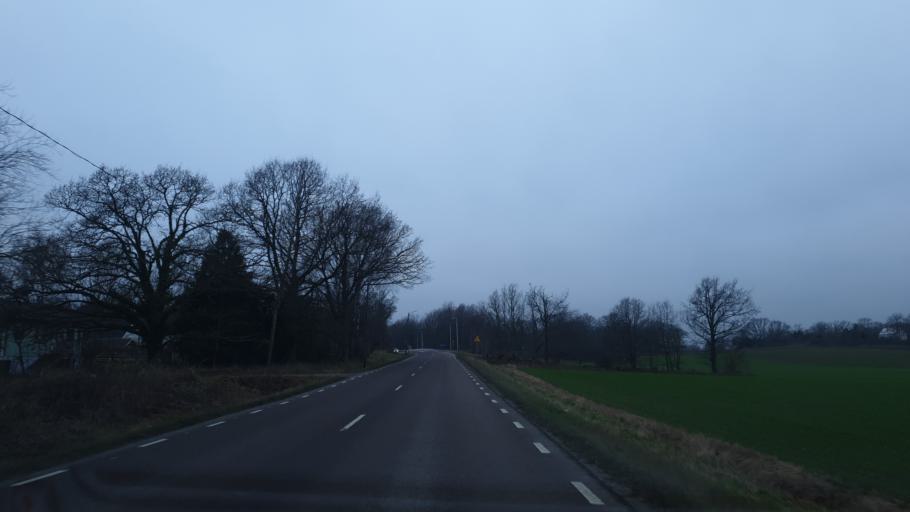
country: SE
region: Blekinge
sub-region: Karlskrona Kommun
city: Jaemjoe
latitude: 56.1689
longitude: 15.7438
